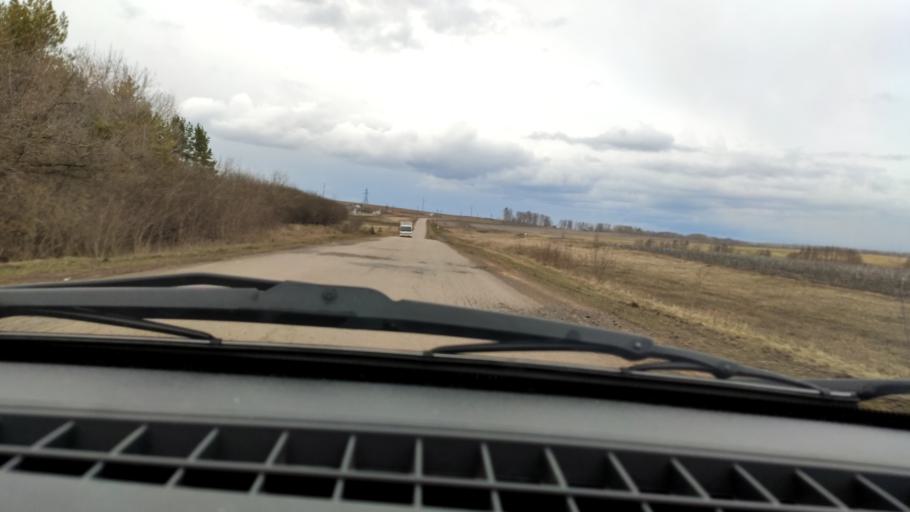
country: RU
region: Bashkortostan
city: Chekmagush
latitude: 55.2320
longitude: 54.5909
